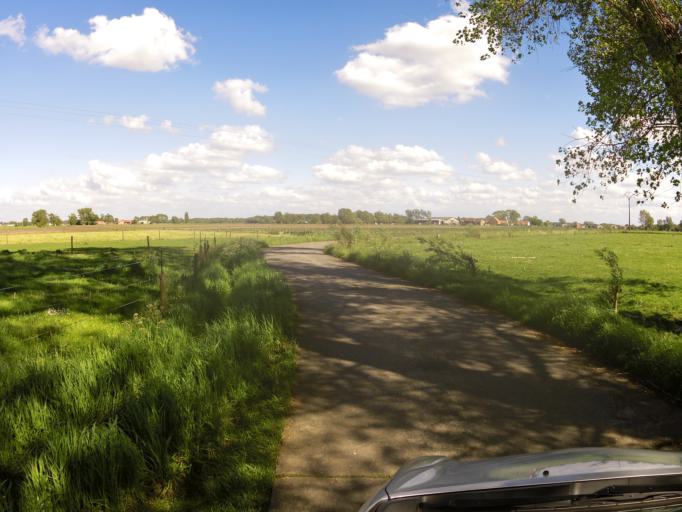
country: BE
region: Flanders
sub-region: Provincie West-Vlaanderen
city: Koekelare
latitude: 51.1142
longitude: 2.9781
